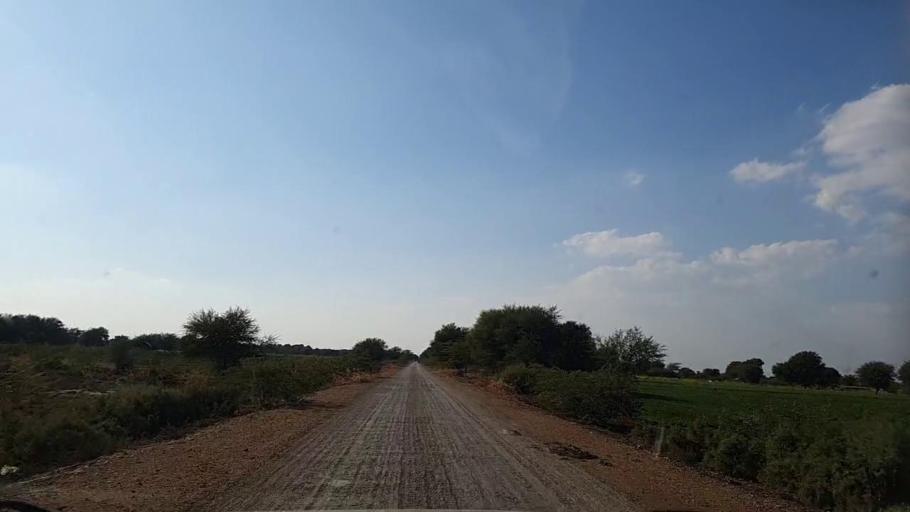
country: PK
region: Sindh
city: Pithoro
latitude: 25.6472
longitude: 69.3300
